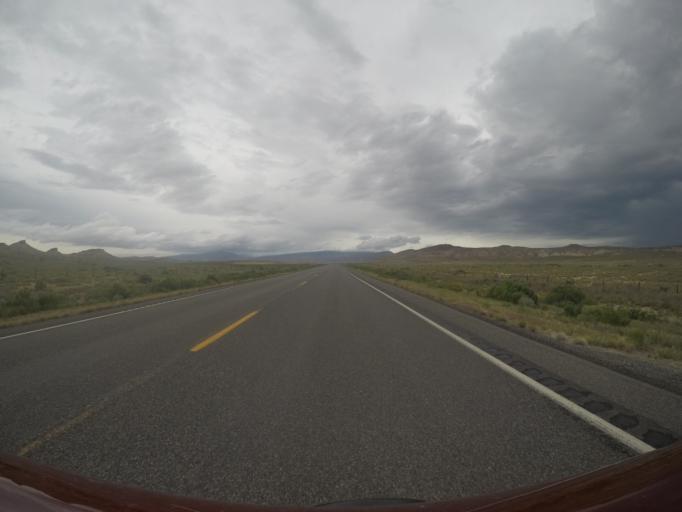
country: US
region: Wyoming
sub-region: Big Horn County
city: Lovell
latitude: 44.9091
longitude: -108.2914
